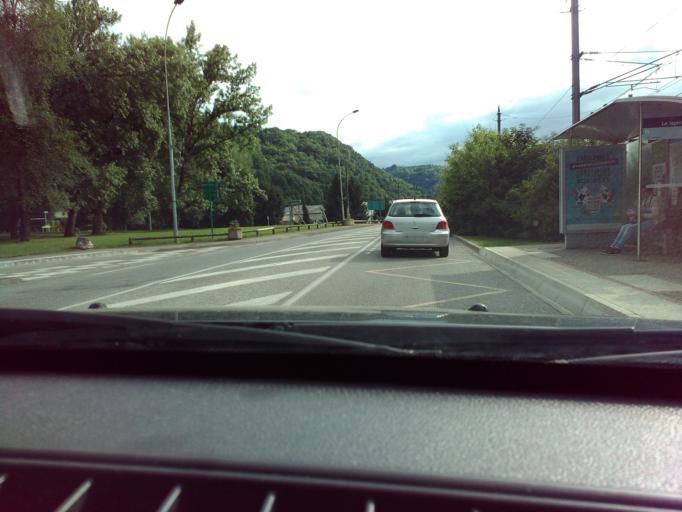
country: FR
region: Rhone-Alpes
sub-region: Departement de l'Isere
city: Gieres
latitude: 45.1875
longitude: 5.8072
